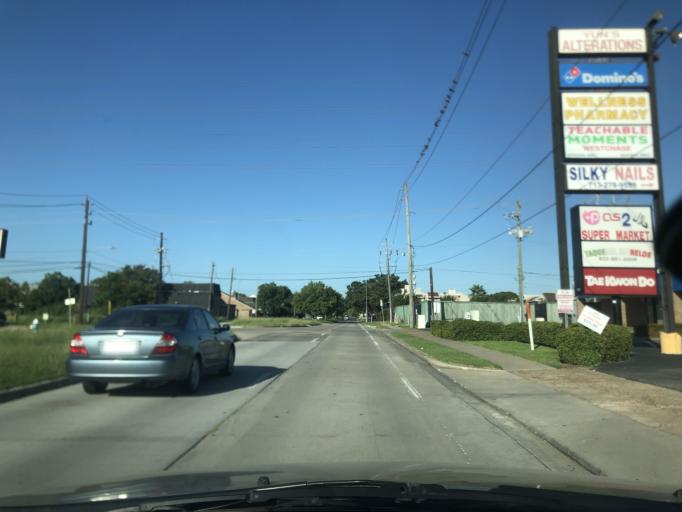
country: US
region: Texas
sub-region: Harris County
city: Bunker Hill Village
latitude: 29.7481
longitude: -95.5728
